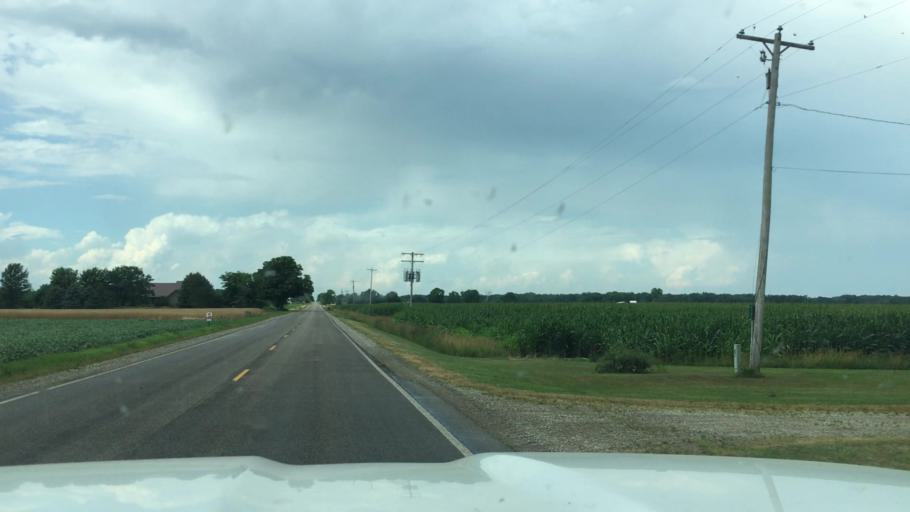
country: US
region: Michigan
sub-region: Montcalm County
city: Carson City
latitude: 43.2223
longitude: -84.7776
